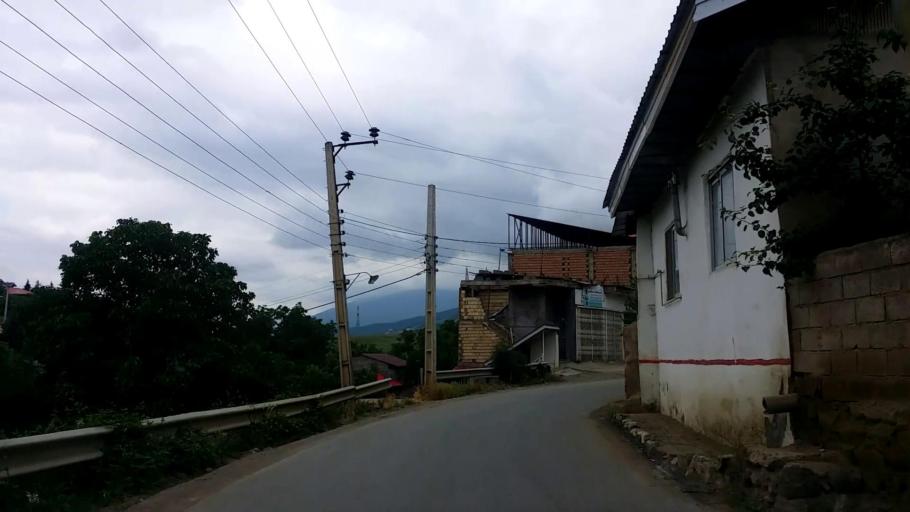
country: IR
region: Mazandaran
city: Chalus
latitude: 36.5151
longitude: 51.2590
